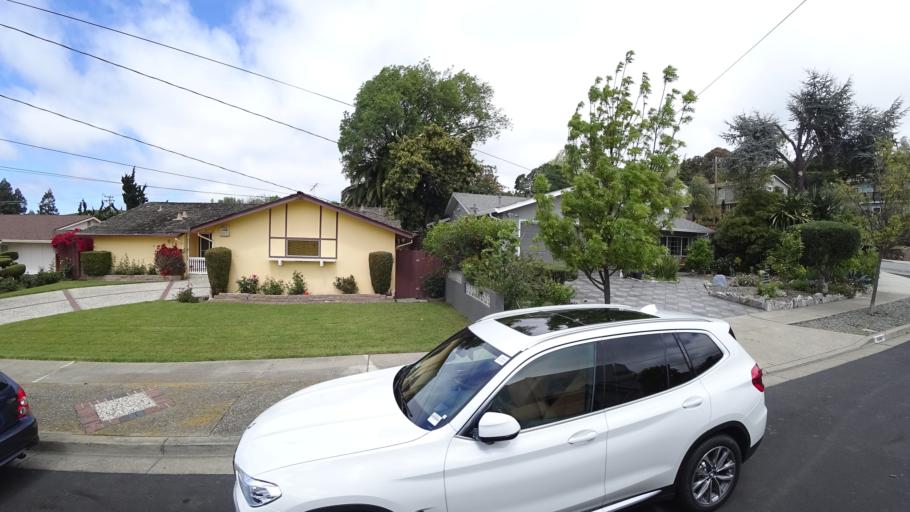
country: US
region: California
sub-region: Alameda County
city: Union City
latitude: 37.6301
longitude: -122.0416
